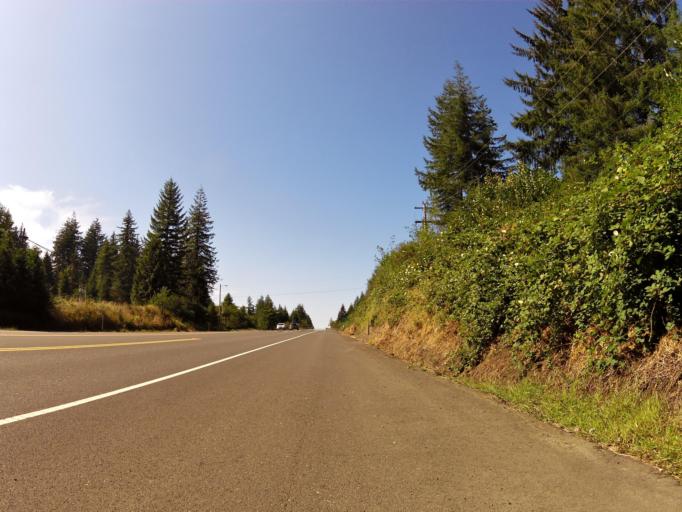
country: US
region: Oregon
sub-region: Clatsop County
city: Astoria
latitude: 46.1664
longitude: -123.6101
